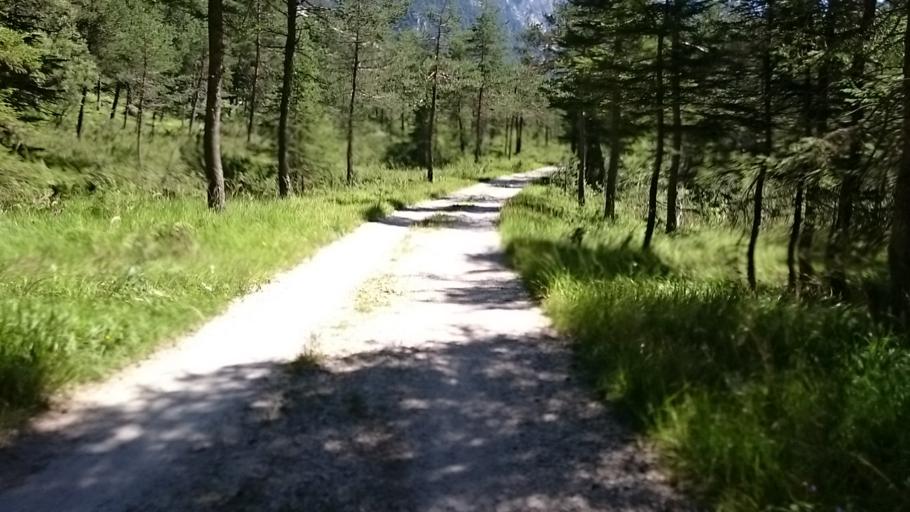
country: IT
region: Veneto
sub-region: Provincia di Belluno
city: San Vito
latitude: 46.4971
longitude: 12.1727
